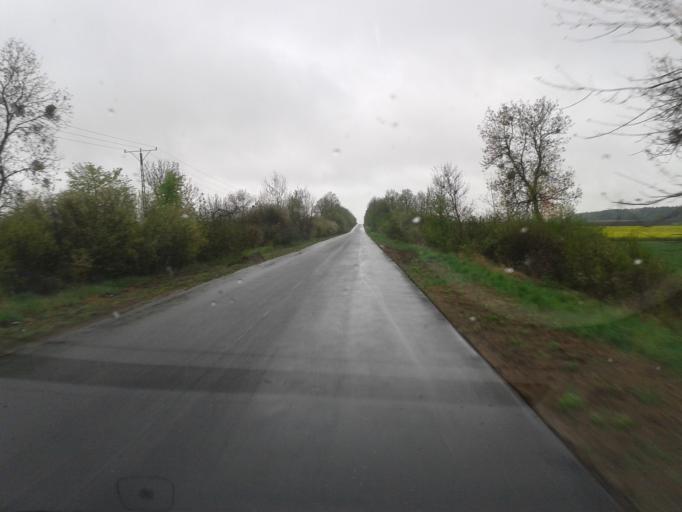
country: UA
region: Lviv
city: Uhniv
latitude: 50.4023
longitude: 23.7009
